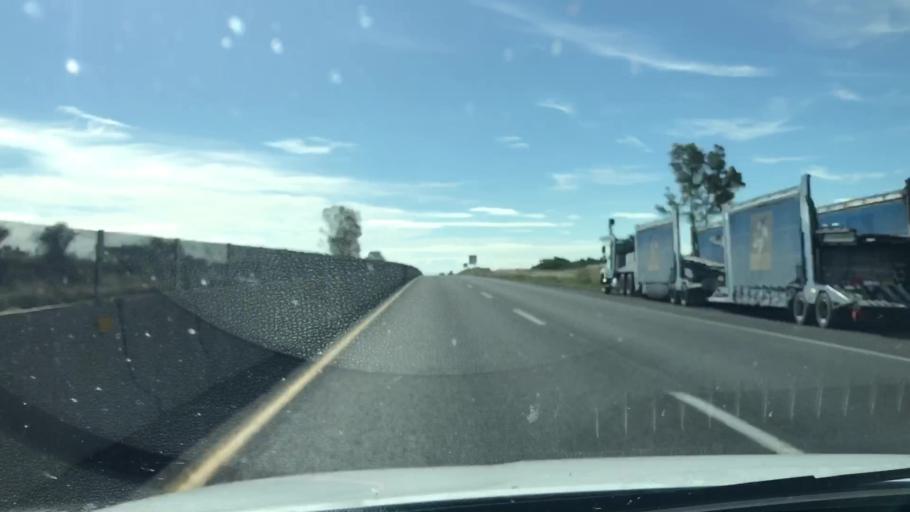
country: MX
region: Guanajuato
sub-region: Leon
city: Rizos de la Joya (Rizos del Saucillo)
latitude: 21.1098
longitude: -101.7928
